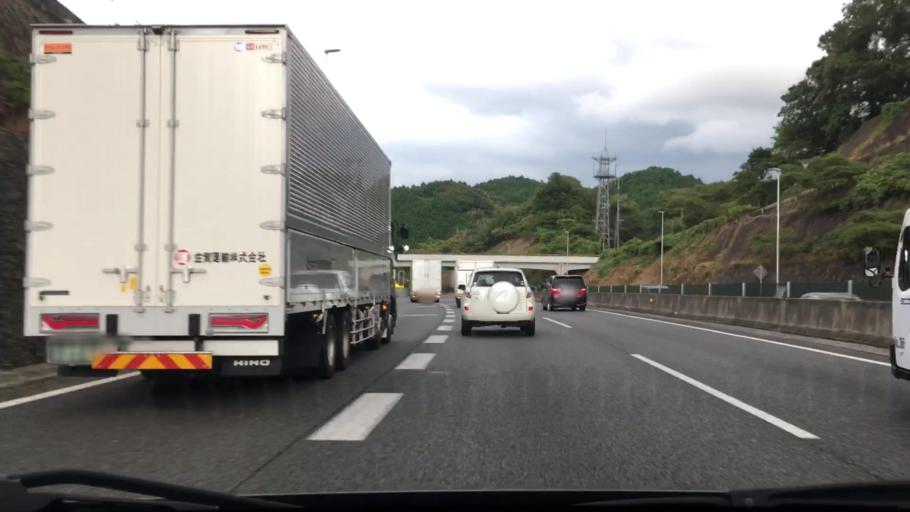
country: JP
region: Fukuoka
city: Nishifukuma
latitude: 33.7491
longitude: 130.5555
